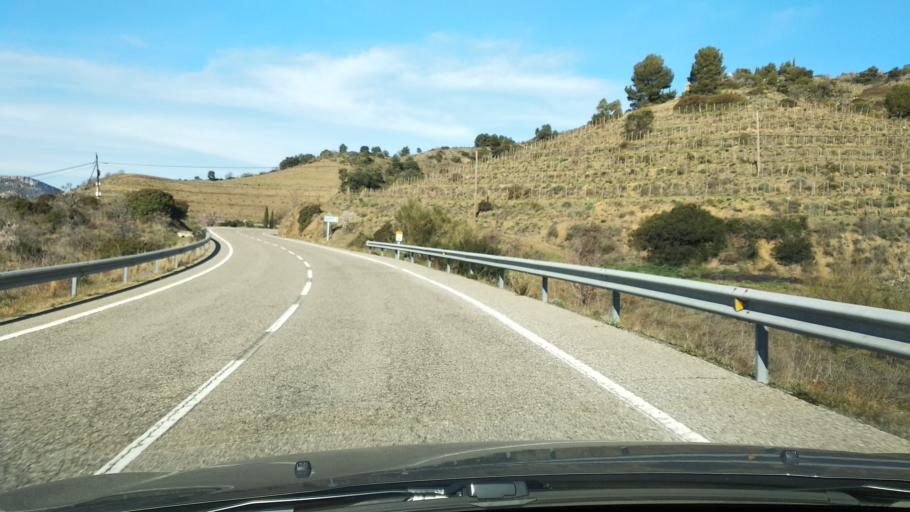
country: ES
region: Catalonia
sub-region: Provincia de Tarragona
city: Falset
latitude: 41.2042
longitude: 0.7808
